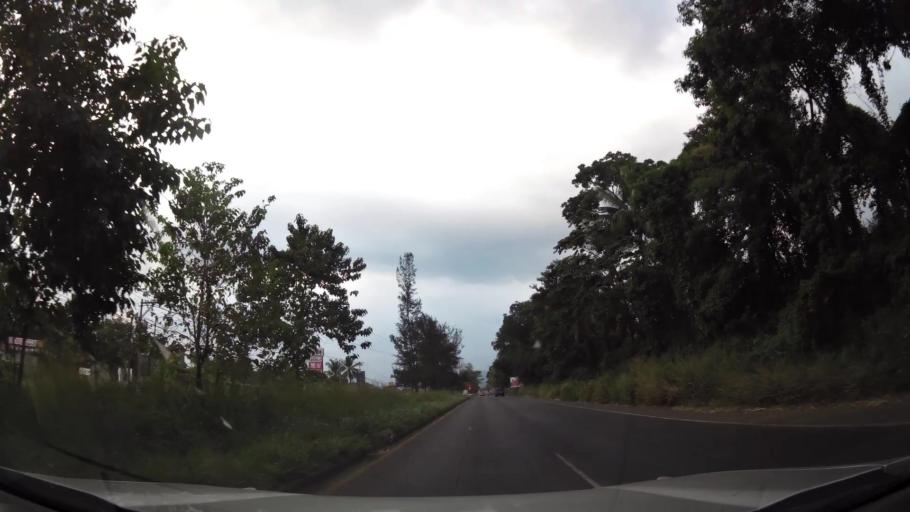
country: GT
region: Escuintla
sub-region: Municipio de Escuintla
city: Escuintla
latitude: 14.2778
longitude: -90.7793
